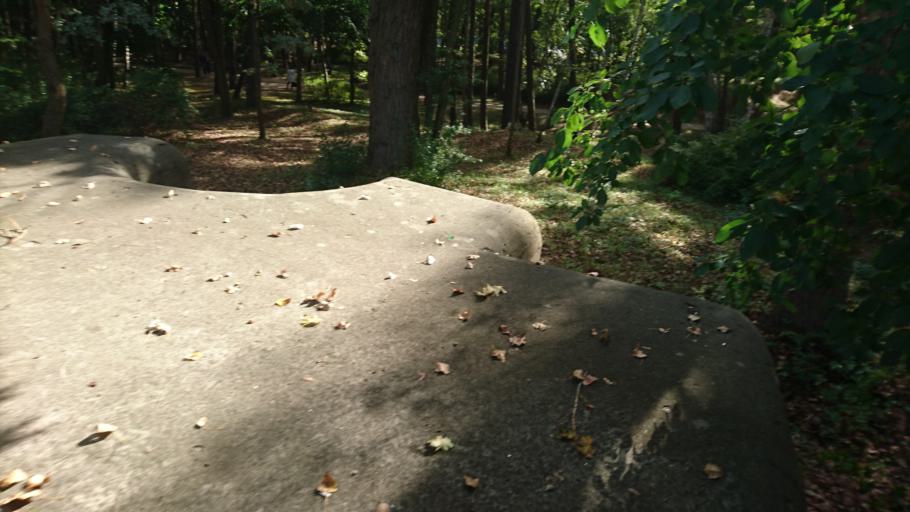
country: PL
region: Pomeranian Voivodeship
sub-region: Gdansk
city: Gdansk
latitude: 54.4077
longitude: 18.6432
